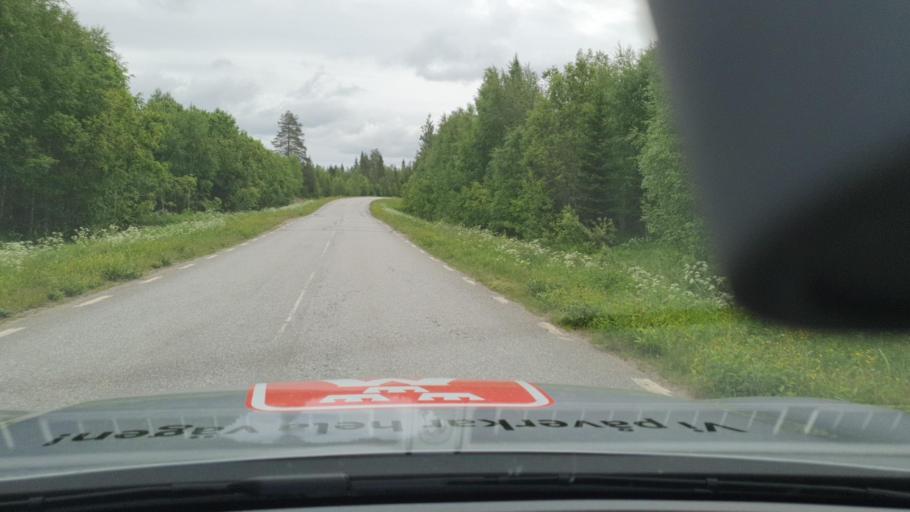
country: SE
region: Norrbotten
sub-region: Lulea Kommun
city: Ranea
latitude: 65.8857
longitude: 22.1975
